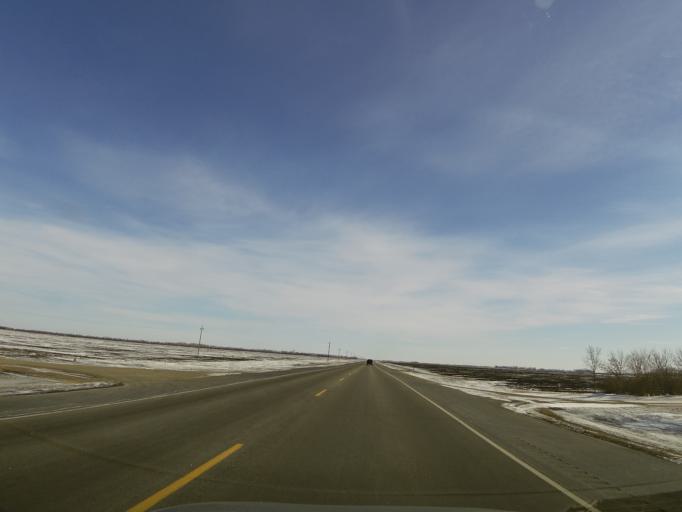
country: US
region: North Dakota
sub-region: Walsh County
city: Grafton
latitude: 48.4124
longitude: -97.3421
